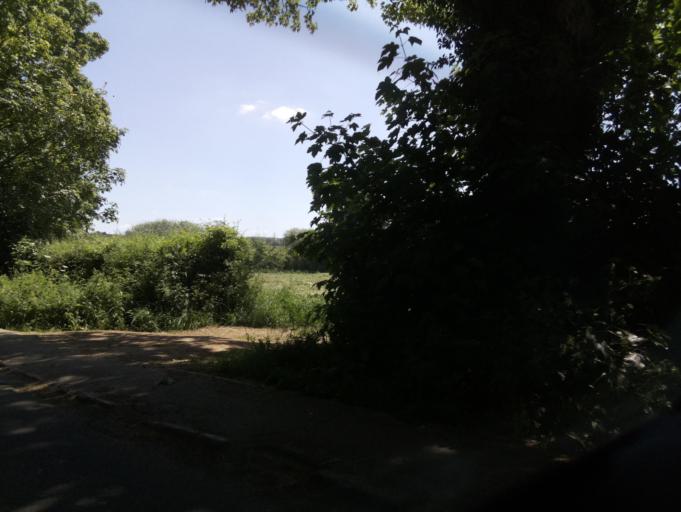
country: GB
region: England
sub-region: Wiltshire
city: Bremhill
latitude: 51.4734
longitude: -2.0561
